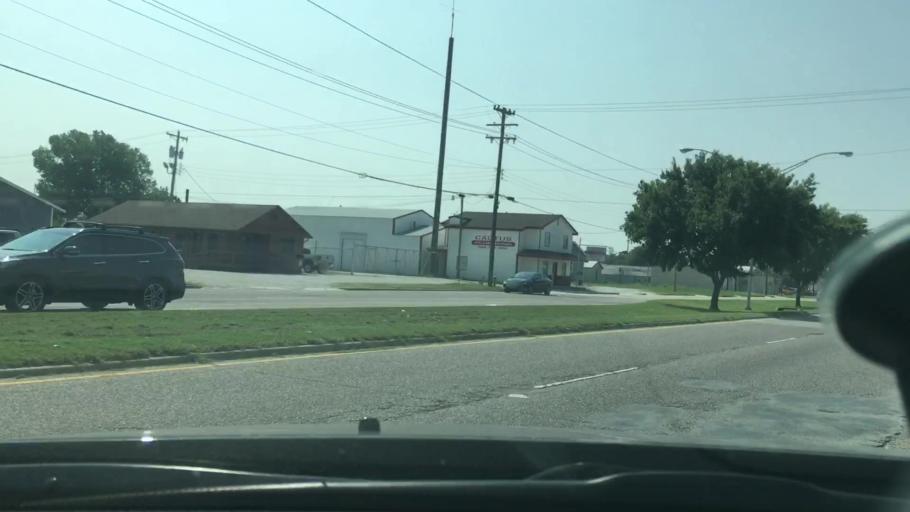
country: US
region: Oklahoma
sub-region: Pontotoc County
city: Ada
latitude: 34.7895
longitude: -96.6788
